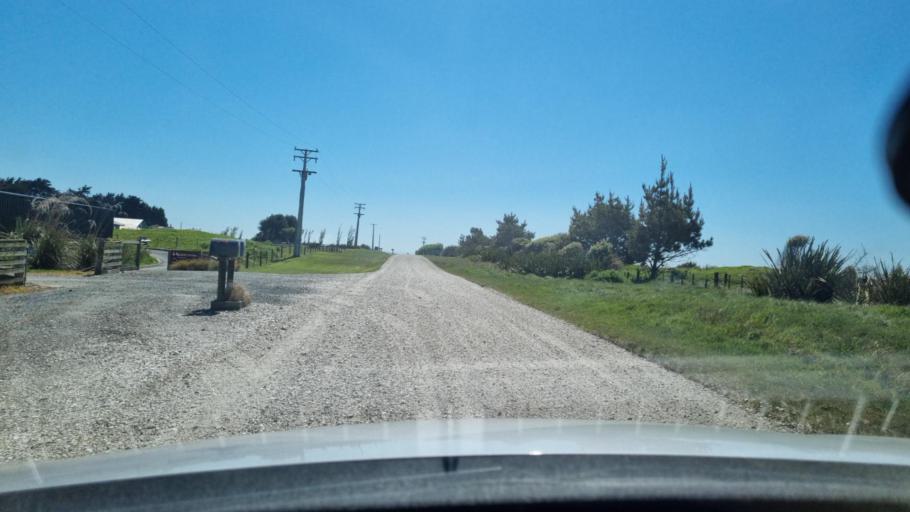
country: NZ
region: Southland
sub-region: Invercargill City
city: Invercargill
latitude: -46.4125
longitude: 168.2634
